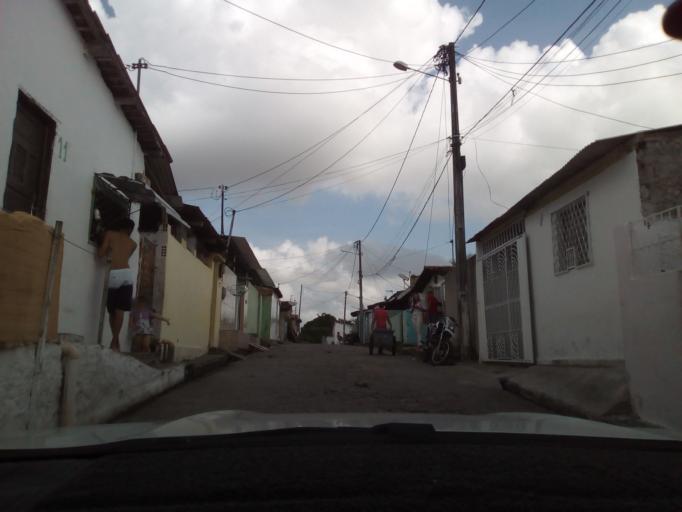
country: BR
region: Paraiba
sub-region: Bayeux
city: Bayeux
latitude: -7.1234
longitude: -34.9271
